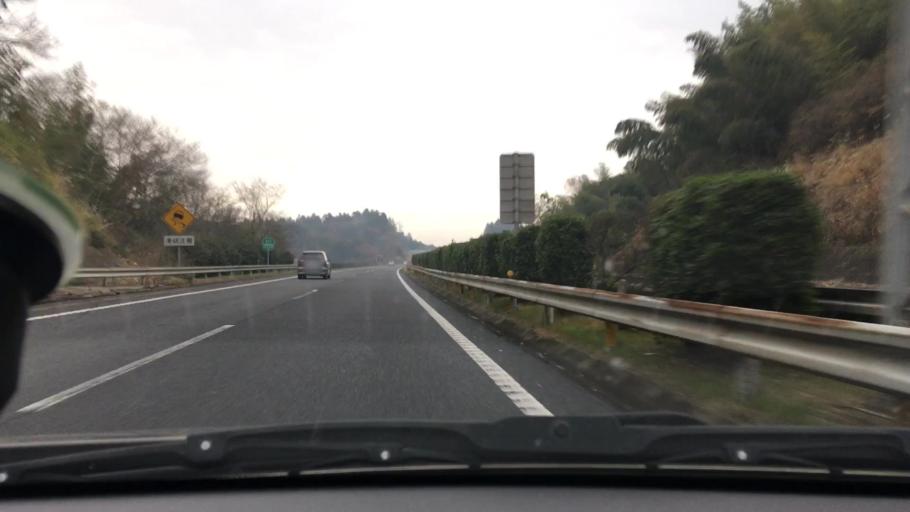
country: JP
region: Chiba
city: Narita
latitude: 35.7916
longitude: 140.3500
